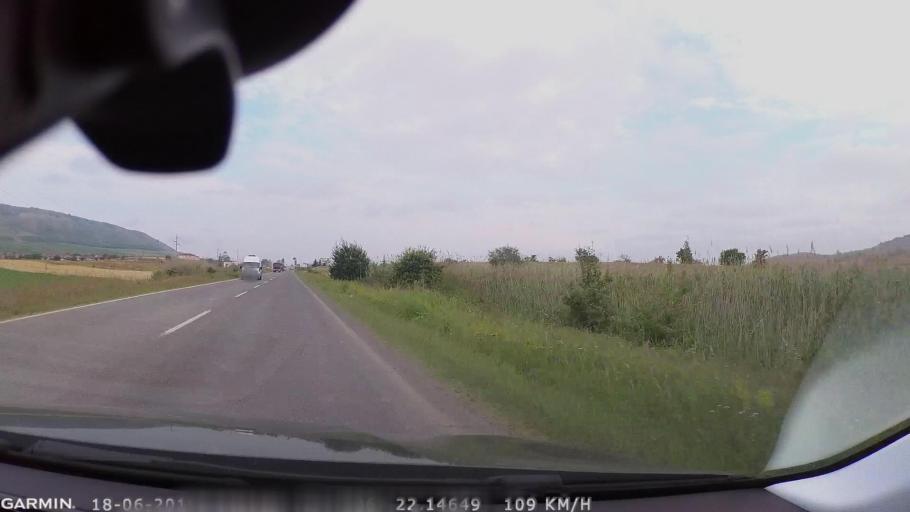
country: MK
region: Stip
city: Shtip
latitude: 41.7712
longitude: 22.1452
